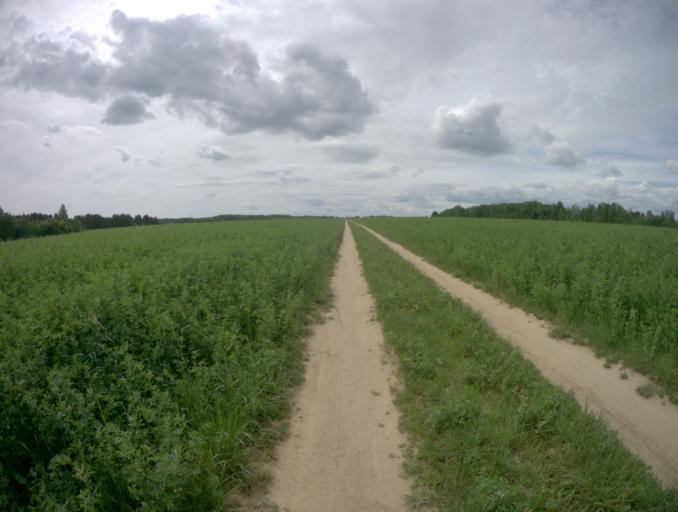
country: RU
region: Vladimir
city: Stavrovo
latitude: 56.2361
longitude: 39.9152
